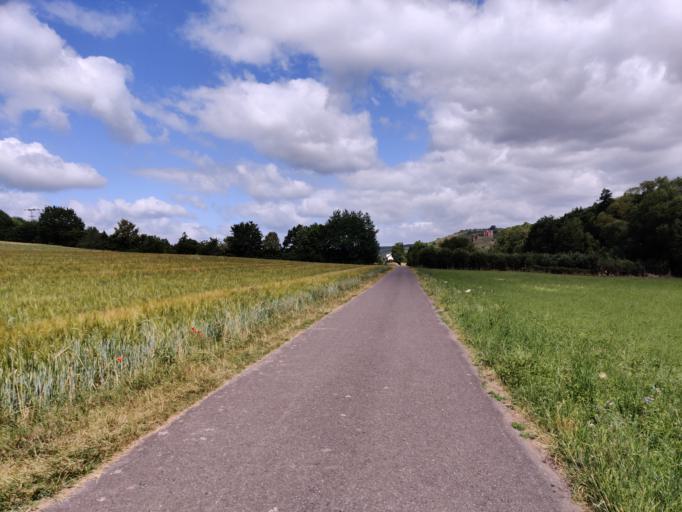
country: DE
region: Rheinland-Pfalz
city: Gutenberg
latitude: 49.8738
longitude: 7.8057
